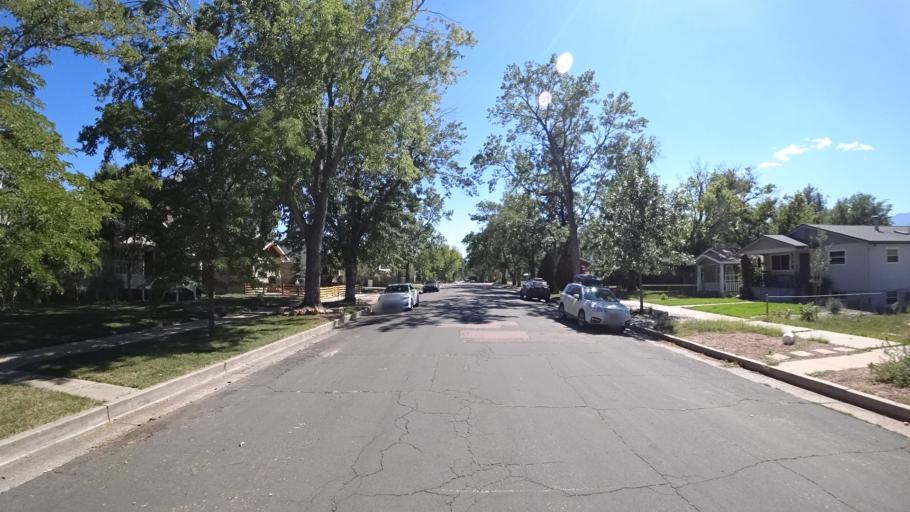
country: US
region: Colorado
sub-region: El Paso County
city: Colorado Springs
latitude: 38.8426
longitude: -104.8048
